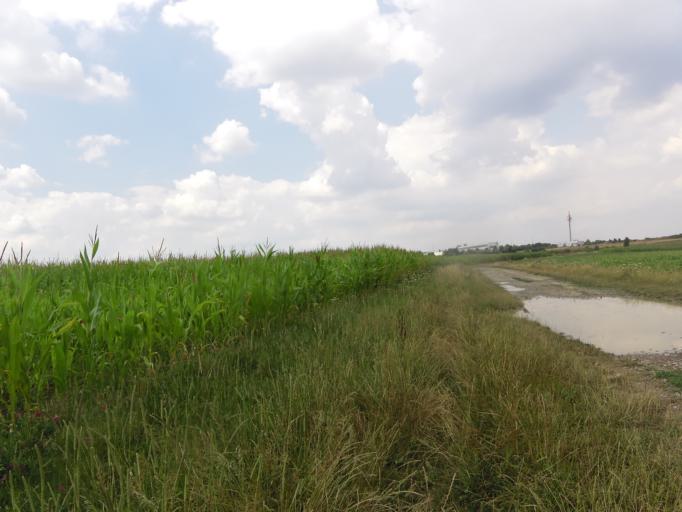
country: DE
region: Bavaria
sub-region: Regierungsbezirk Unterfranken
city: Eibelstadt
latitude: 49.7294
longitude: 9.9736
